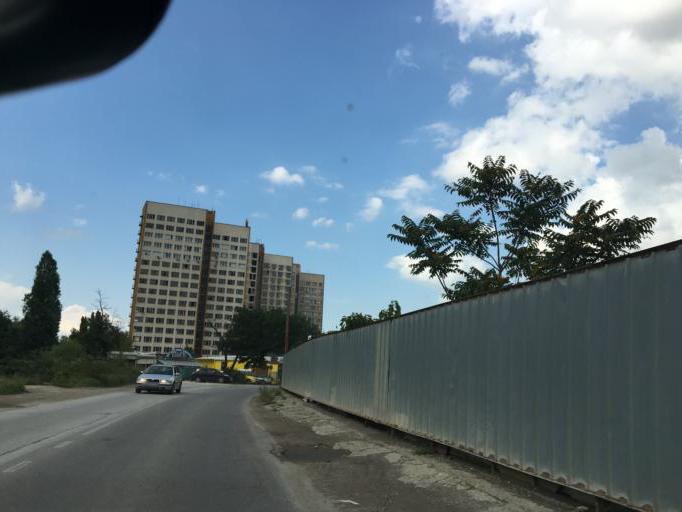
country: BG
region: Sofia-Capital
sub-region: Stolichna Obshtina
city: Sofia
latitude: 42.6455
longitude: 23.3538
